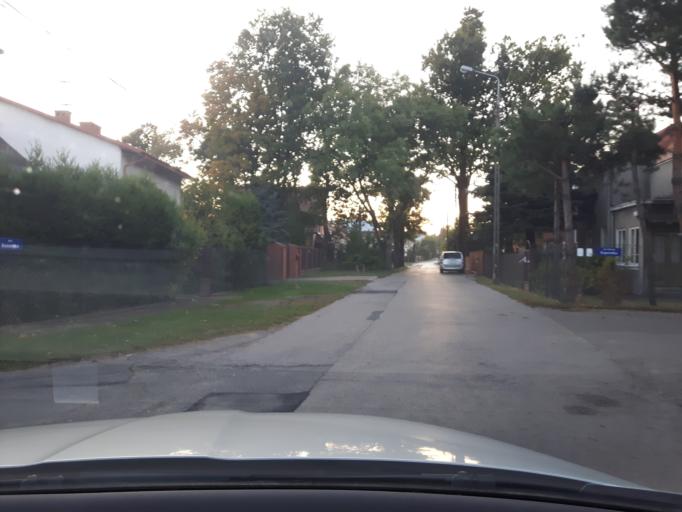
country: PL
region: Masovian Voivodeship
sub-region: Powiat wolominski
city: Kobylka
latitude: 52.3336
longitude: 21.1908
